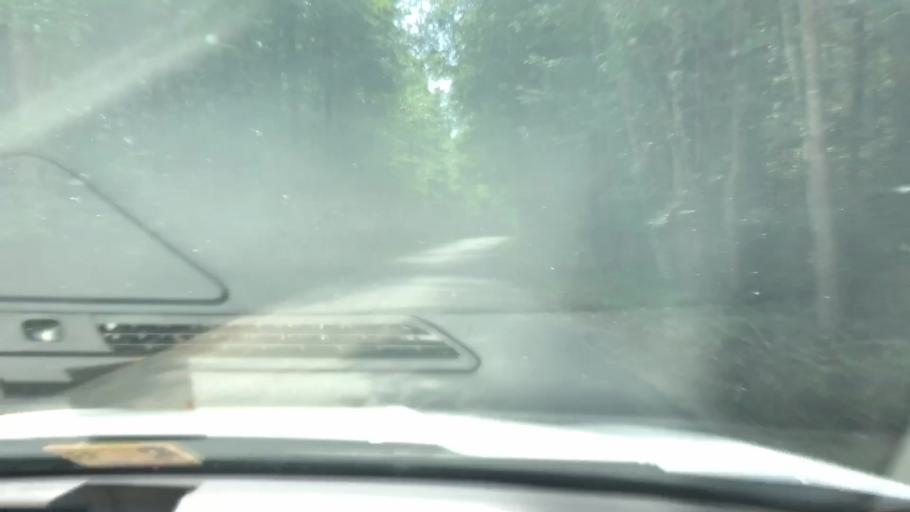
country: US
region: Virginia
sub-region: Charles City County
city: Charles City
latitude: 37.3554
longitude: -77.0004
